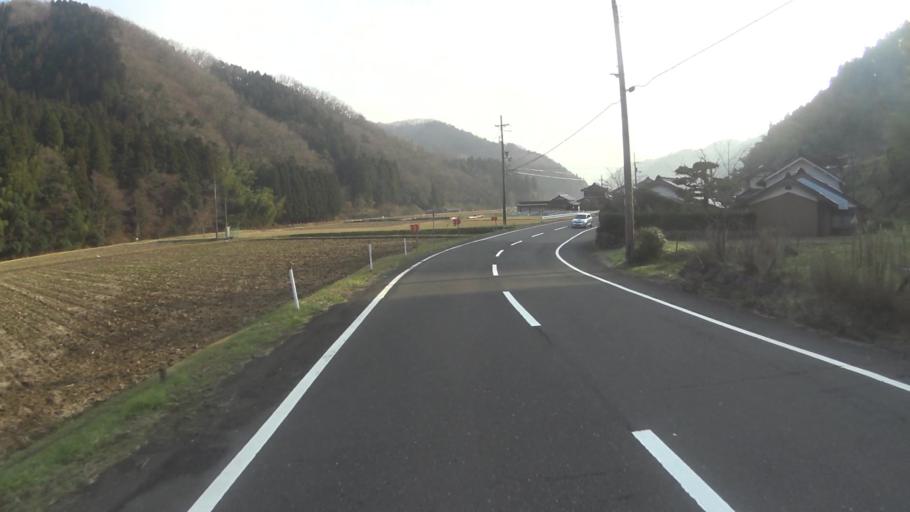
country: JP
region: Kyoto
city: Maizuru
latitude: 35.4019
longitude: 135.4156
